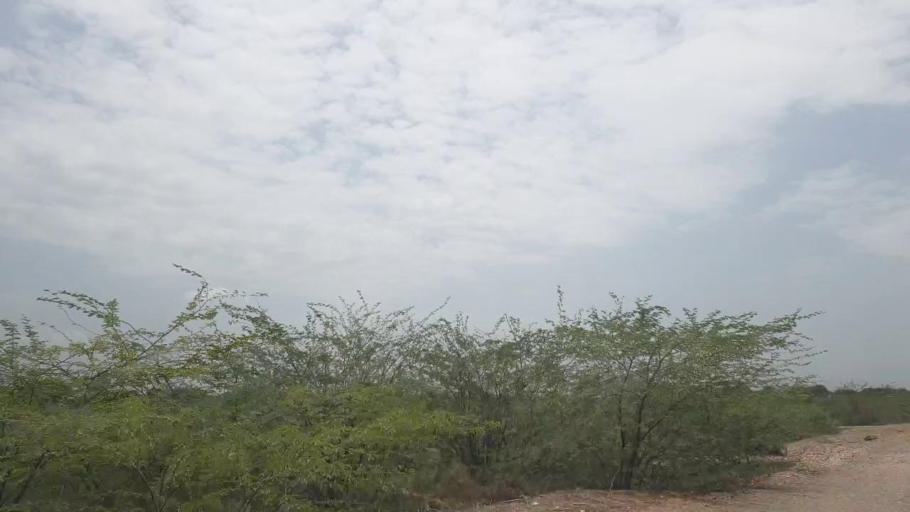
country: PK
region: Sindh
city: Naukot
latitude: 24.9150
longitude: 69.2104
